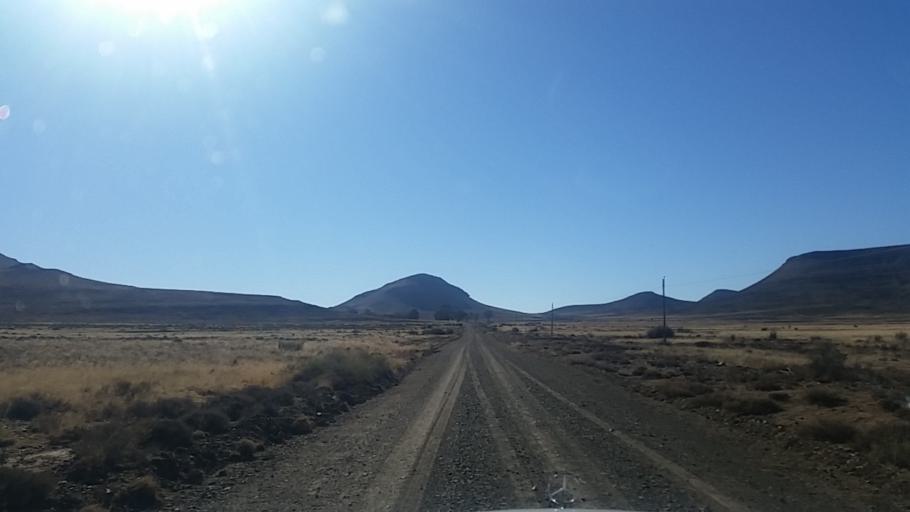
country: ZA
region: Eastern Cape
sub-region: Chris Hani District Municipality
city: Middelburg
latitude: -31.7971
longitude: 24.7162
